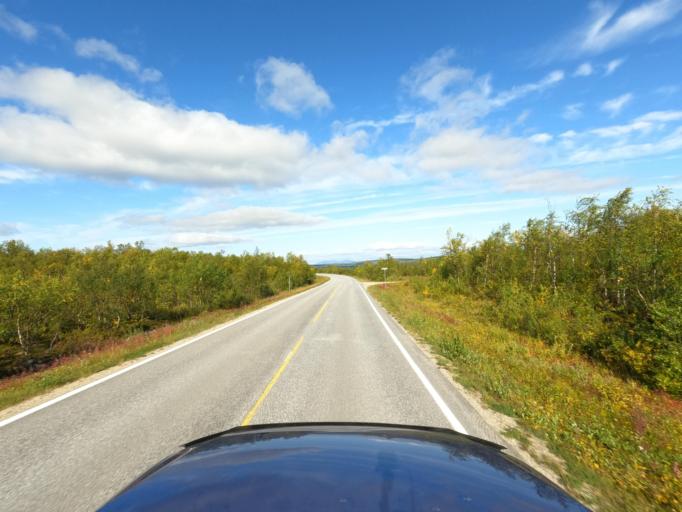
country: NO
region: Finnmark Fylke
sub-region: Karasjok
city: Karasjohka
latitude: 69.6026
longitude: 25.3274
